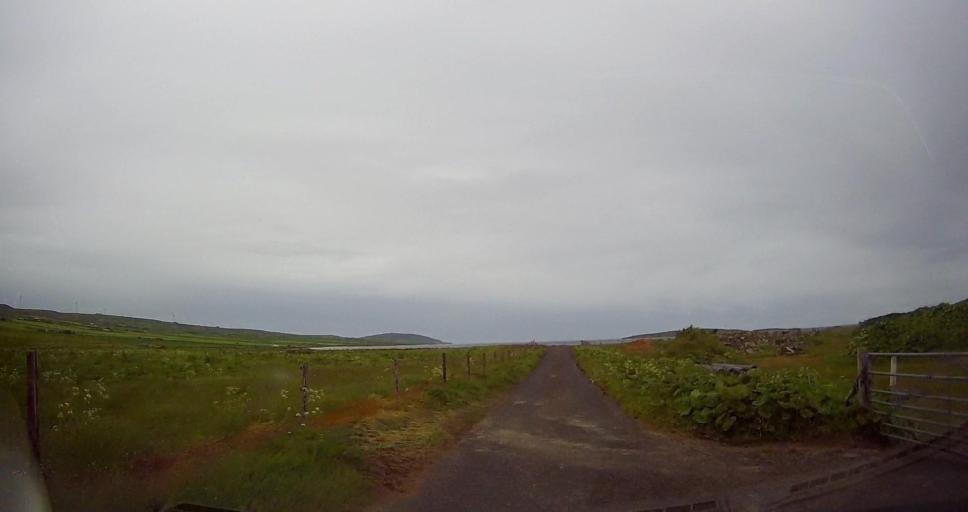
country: GB
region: Scotland
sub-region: Orkney Islands
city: Orkney
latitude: 59.1176
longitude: -3.0846
